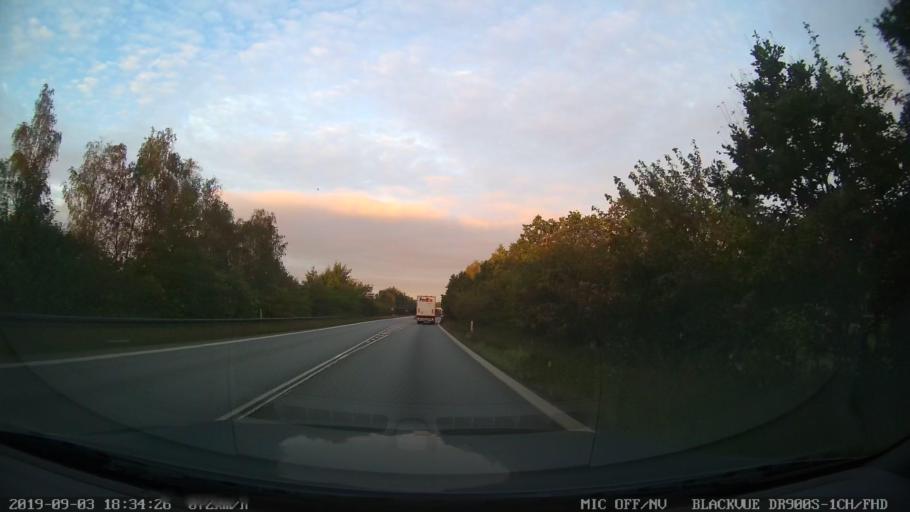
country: DK
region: Capital Region
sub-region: Helsingor Kommune
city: Espergaerde
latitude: 56.0070
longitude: 12.5350
